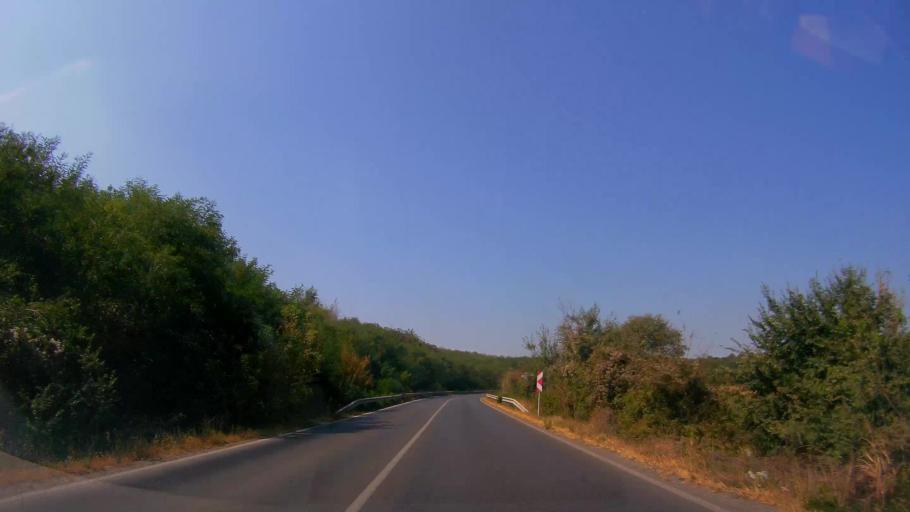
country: BG
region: Razgrad
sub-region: Obshtina Tsar Kaloyan
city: Tsar Kaloyan
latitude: 43.6148
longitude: 26.2169
